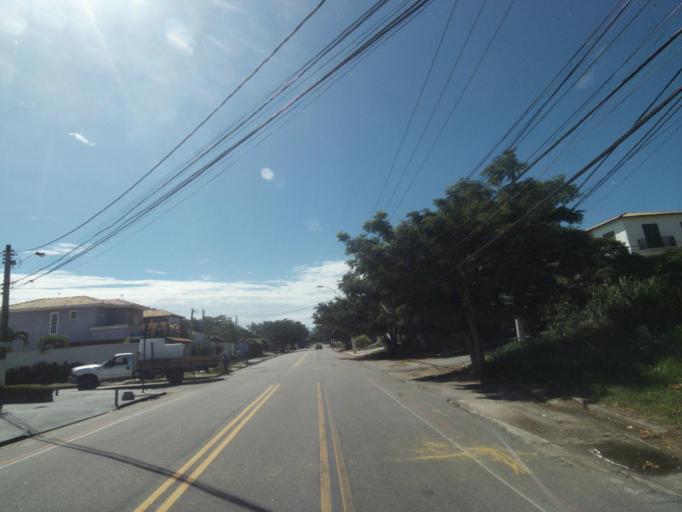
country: BR
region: Rio de Janeiro
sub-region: Niteroi
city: Niteroi
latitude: -22.9529
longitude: -43.0806
